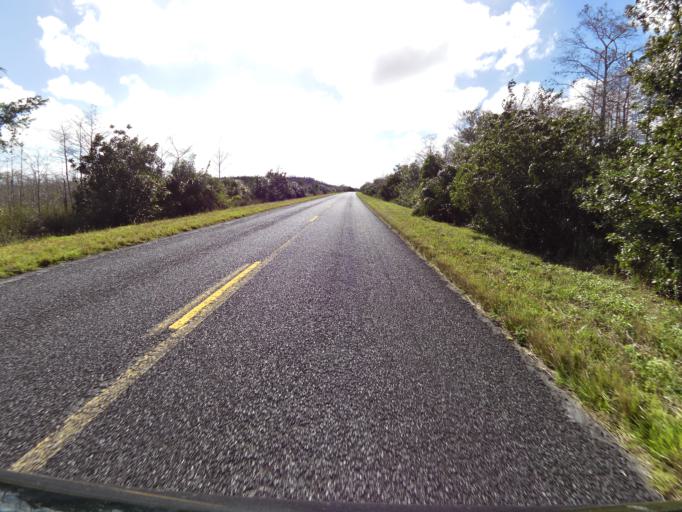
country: US
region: Florida
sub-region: Miami-Dade County
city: Florida City
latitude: 25.4159
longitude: -80.7807
